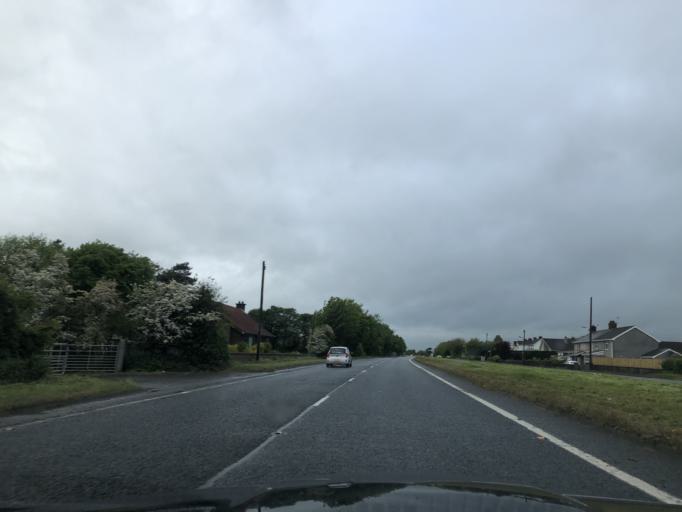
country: GB
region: Northern Ireland
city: Randalstown
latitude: 54.7556
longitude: -6.2413
